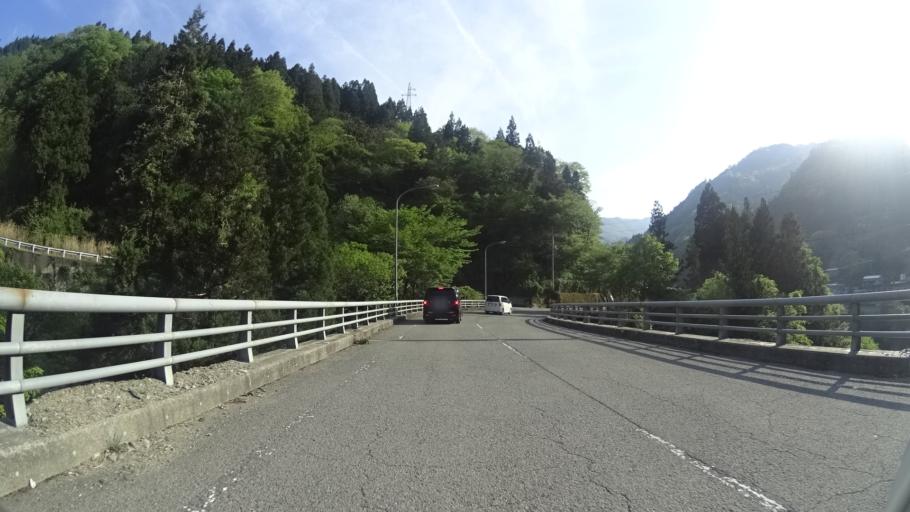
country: JP
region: Tokushima
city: Ikedacho
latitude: 33.8676
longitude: 133.9058
